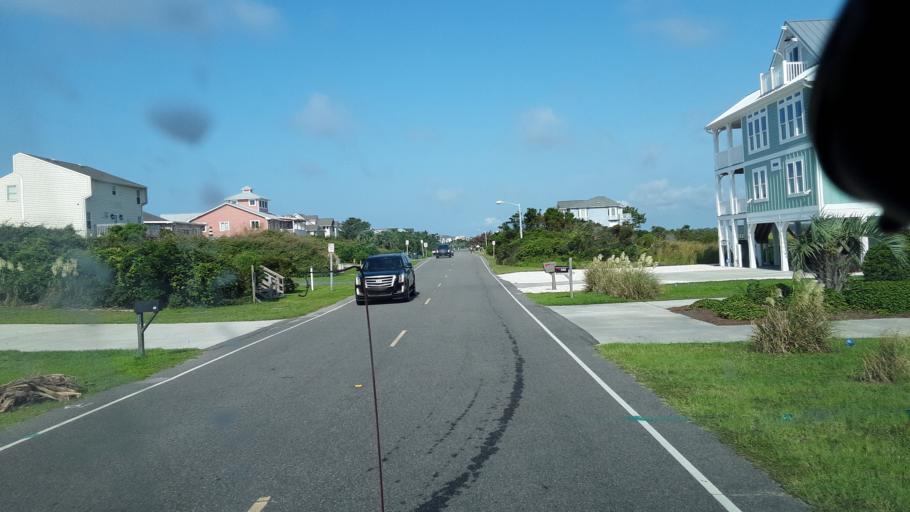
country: US
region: North Carolina
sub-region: Brunswick County
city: Southport
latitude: 33.8934
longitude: -78.0383
